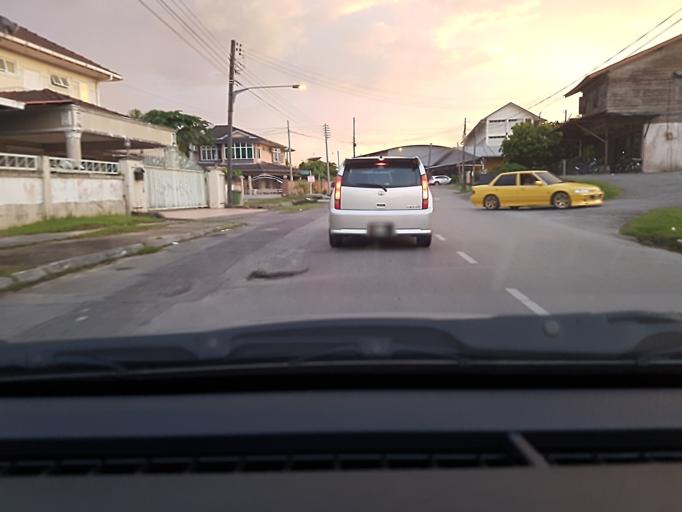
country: MY
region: Sarawak
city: Kuching
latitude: 1.4901
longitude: 110.3213
